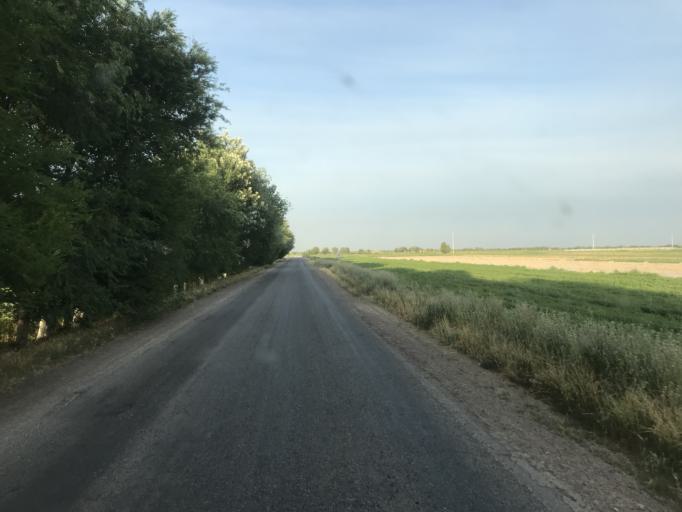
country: KZ
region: Ongtustik Qazaqstan
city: Asykata
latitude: 40.9512
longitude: 68.4492
